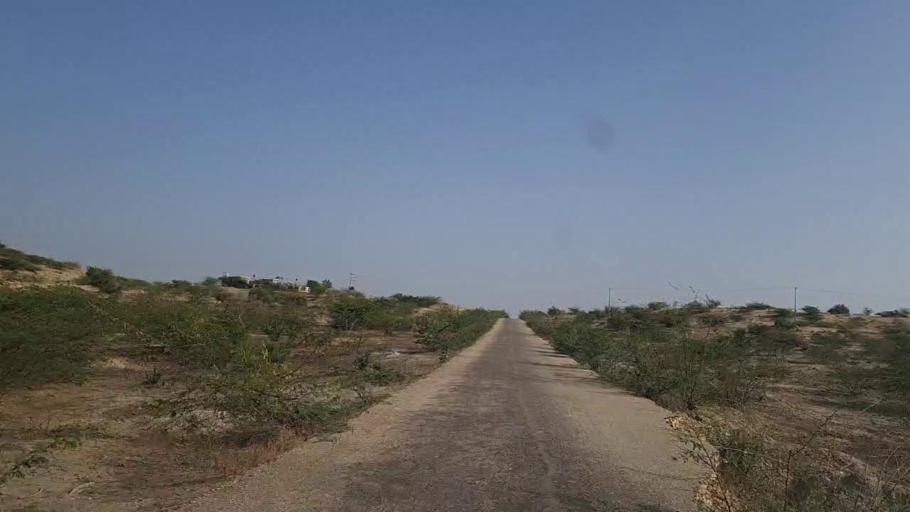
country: PK
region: Sindh
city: Naukot
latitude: 24.6253
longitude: 69.3673
